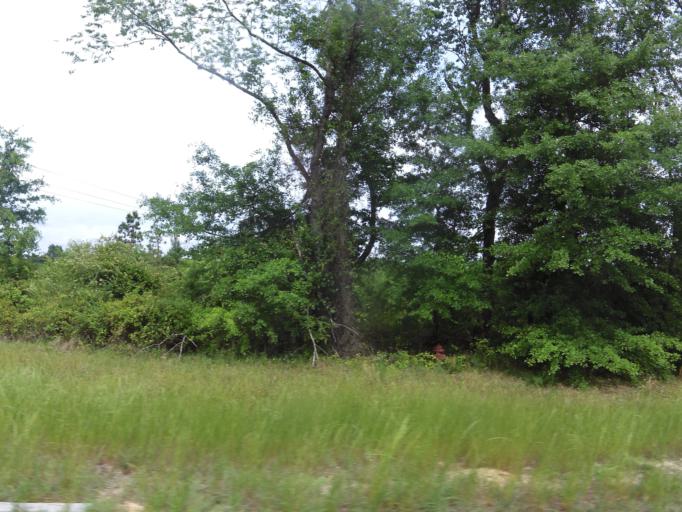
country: US
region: Georgia
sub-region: Jefferson County
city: Wrens
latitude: 33.2292
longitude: -82.4050
